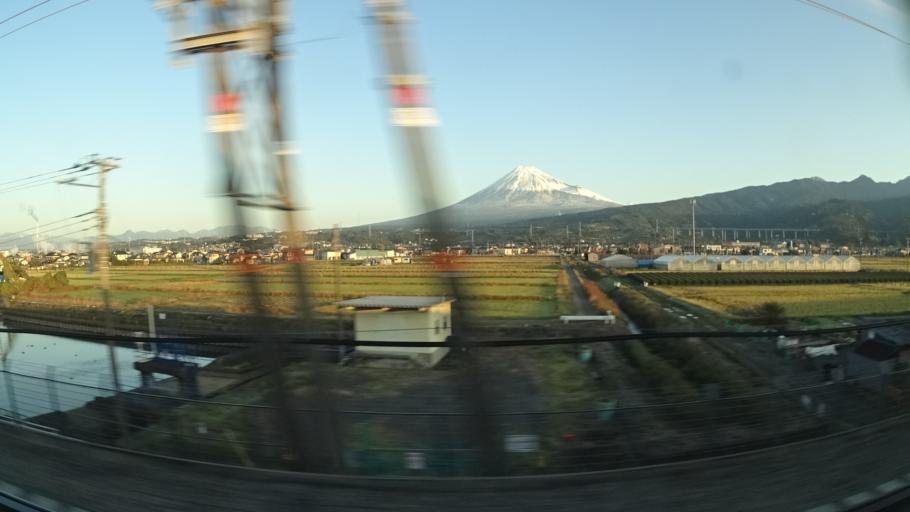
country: JP
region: Shizuoka
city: Fuji
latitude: 35.1538
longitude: 138.7337
